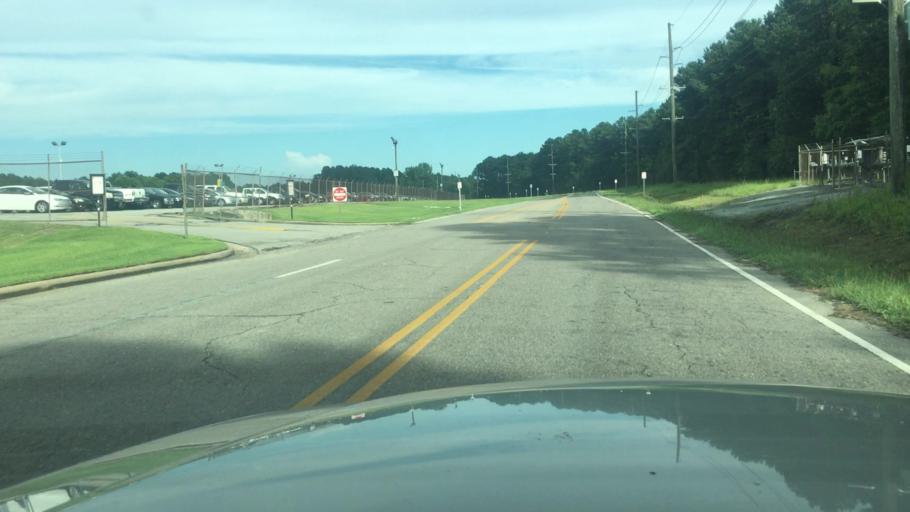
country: US
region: North Carolina
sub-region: Cumberland County
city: Eastover
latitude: 35.1667
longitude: -78.8604
